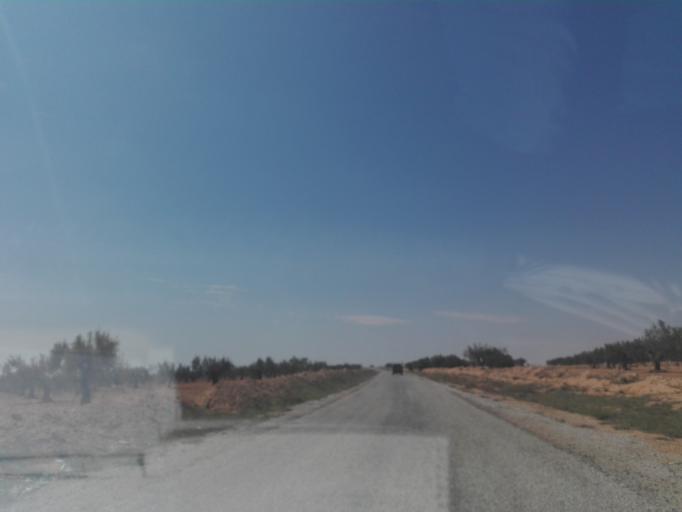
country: TN
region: Safaqis
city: Bi'r `Ali Bin Khalifah
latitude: 34.6461
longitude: 10.4104
